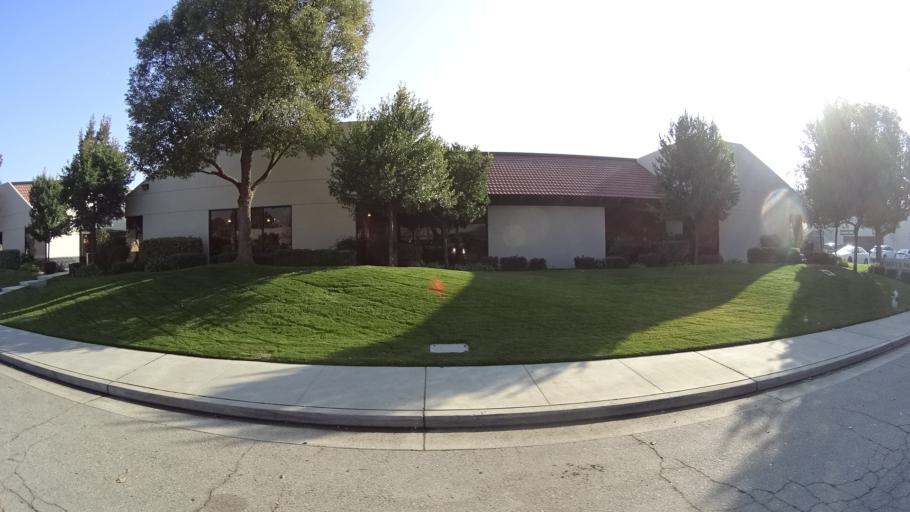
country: US
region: California
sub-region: Kern County
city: Bakersfield
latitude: 35.3655
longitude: -119.0626
